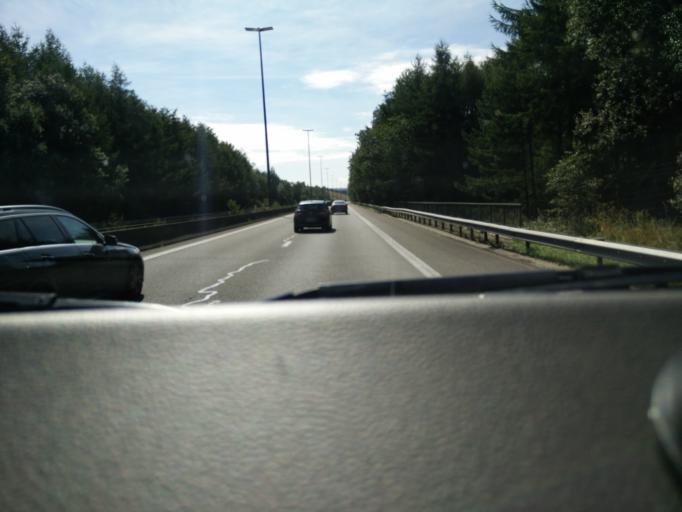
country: BE
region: Wallonia
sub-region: Province du Luxembourg
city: Libin
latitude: 49.9909
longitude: 5.2314
